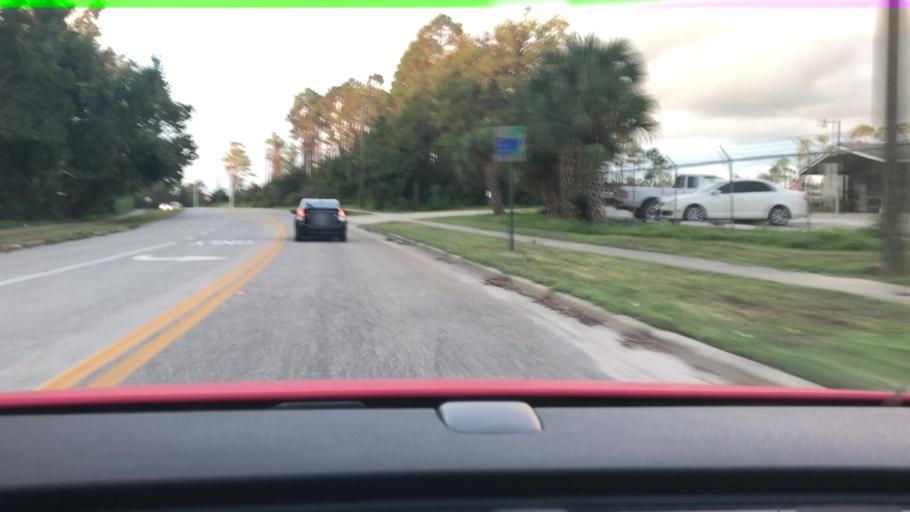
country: US
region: Florida
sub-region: Volusia County
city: South Daytona
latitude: 29.1534
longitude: -81.0220
